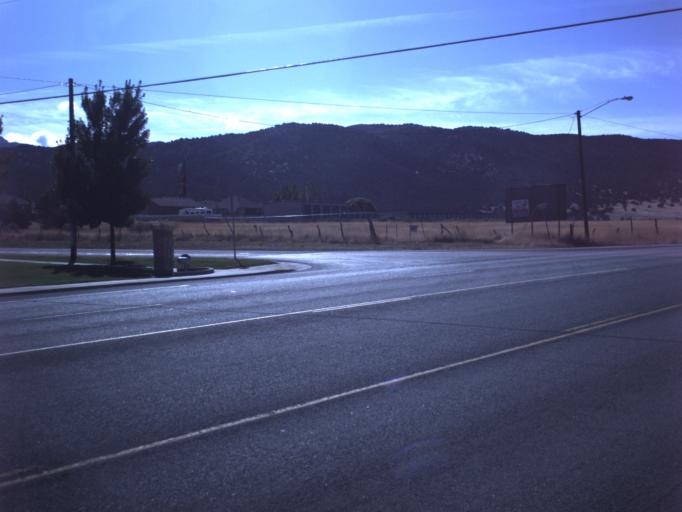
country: US
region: Utah
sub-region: Juab County
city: Nephi
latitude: 39.6902
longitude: -111.8362
